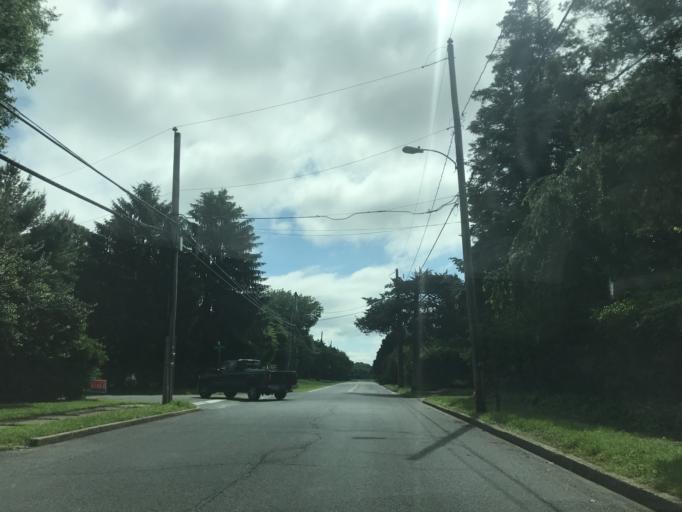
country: US
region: Maryland
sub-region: Caroline County
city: Ridgely
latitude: 38.9169
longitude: -75.9381
